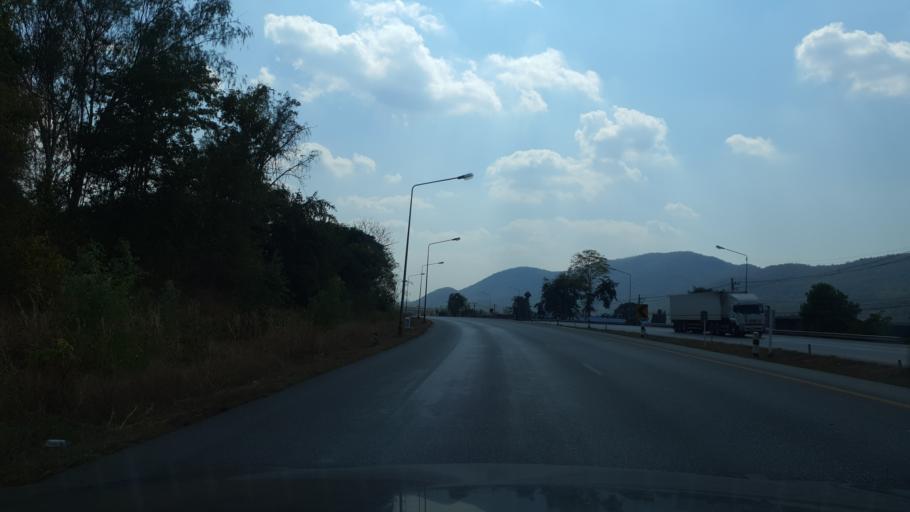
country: TH
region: Lampang
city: Mae Phrik
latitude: 17.3638
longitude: 99.1468
